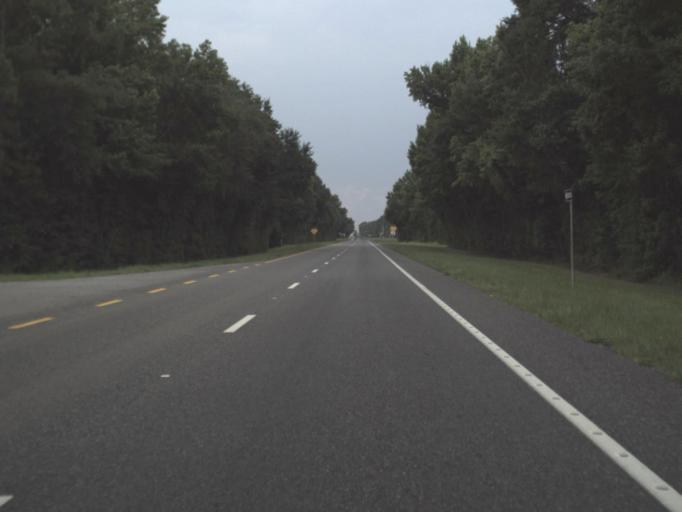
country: US
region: Florida
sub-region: Levy County
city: Williston Highlands
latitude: 29.2588
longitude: -82.7271
